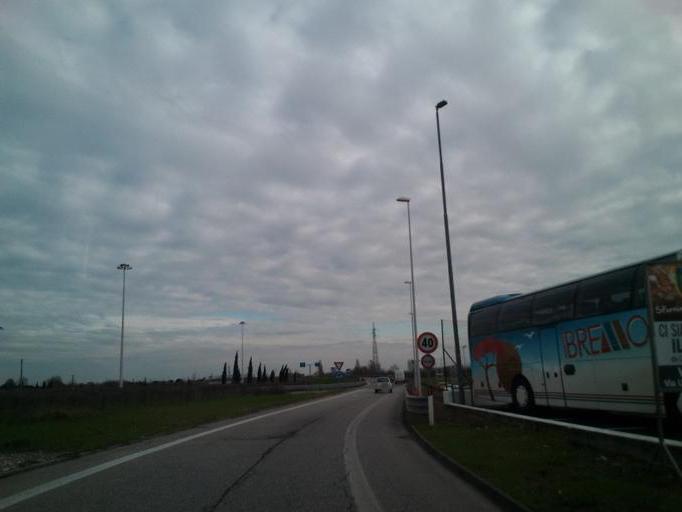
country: IT
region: Veneto
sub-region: Provincia di Verona
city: Montorio
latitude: 45.4296
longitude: 11.0615
